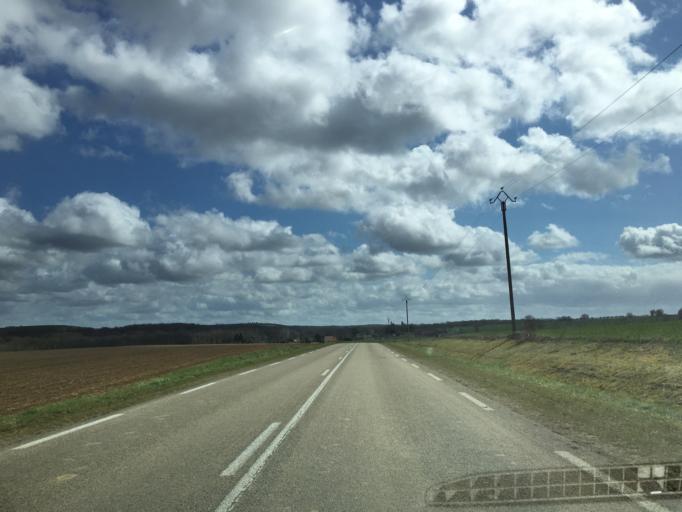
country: FR
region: Bourgogne
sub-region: Departement de l'Yonne
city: Aillant-sur-Tholon
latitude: 47.8477
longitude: 3.3846
